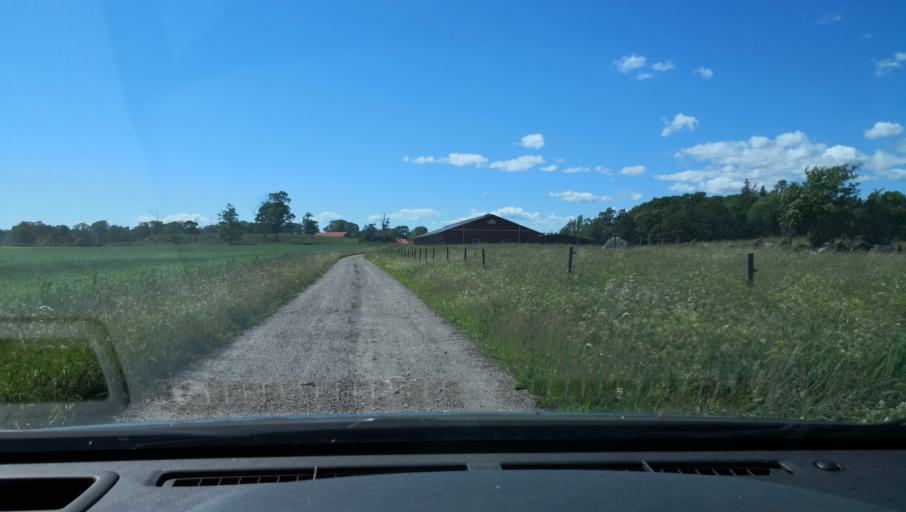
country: SE
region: Soedermanland
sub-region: Eskilstuna Kommun
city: Hallbybrunn
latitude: 59.2975
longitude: 16.3741
